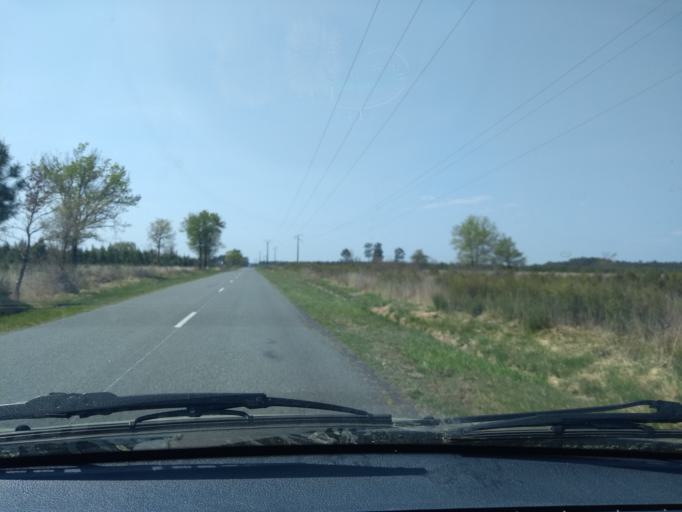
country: FR
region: Aquitaine
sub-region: Departement de la Gironde
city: Belin-Beliet
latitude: 44.5279
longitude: -0.6989
